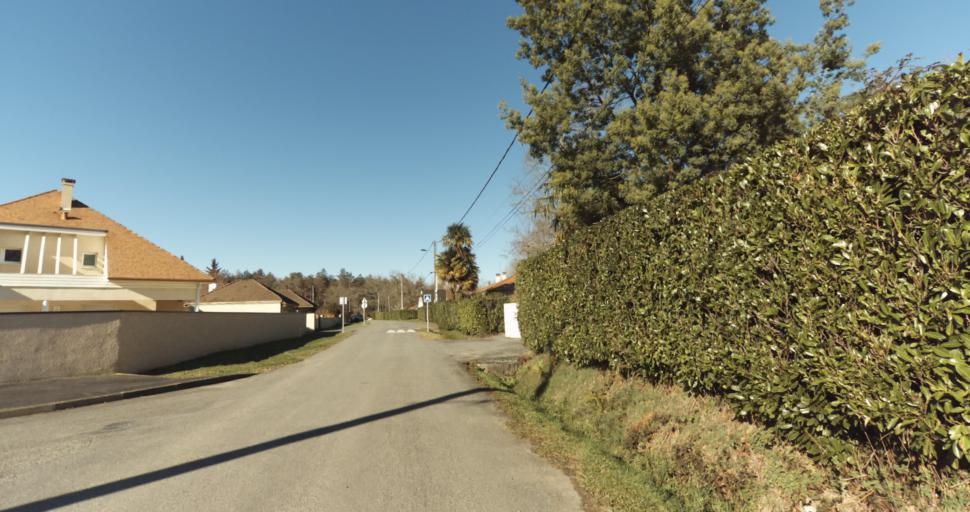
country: FR
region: Aquitaine
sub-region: Departement des Pyrenees-Atlantiques
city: Buros
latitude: 43.3297
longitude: -0.2875
